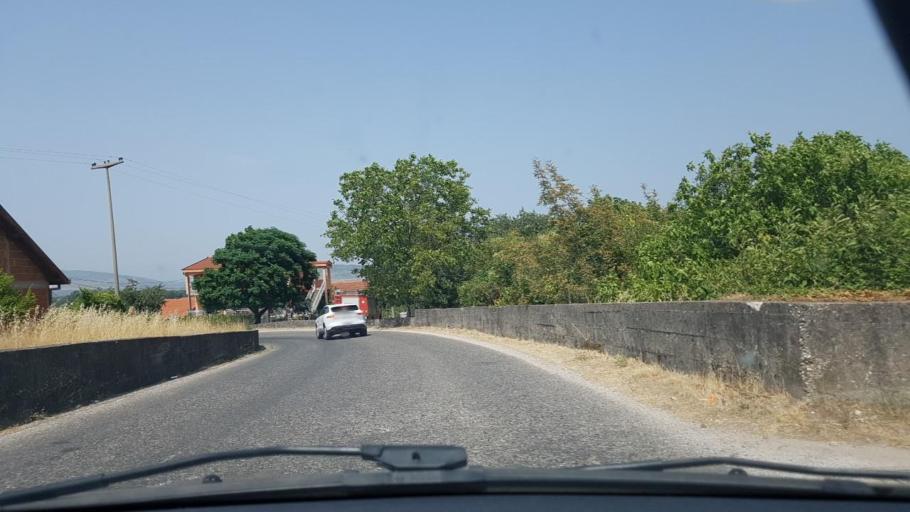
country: HR
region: Dubrovacko-Neretvanska
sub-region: Grad Dubrovnik
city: Metkovic
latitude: 43.0509
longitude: 17.7014
